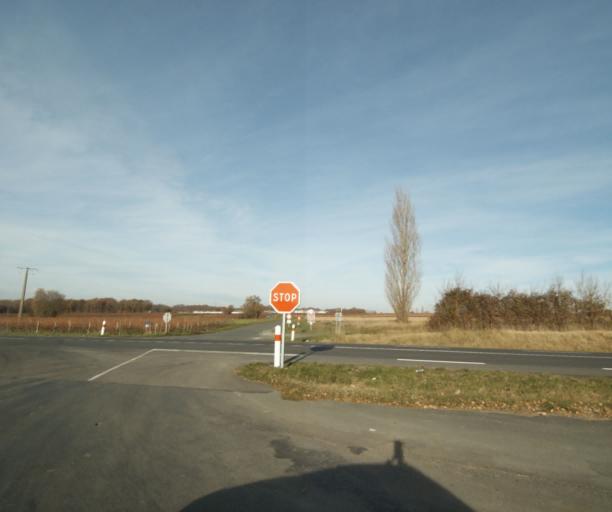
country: FR
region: Poitou-Charentes
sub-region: Departement de la Charente-Maritime
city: Chaniers
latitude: 45.7291
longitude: -0.5273
